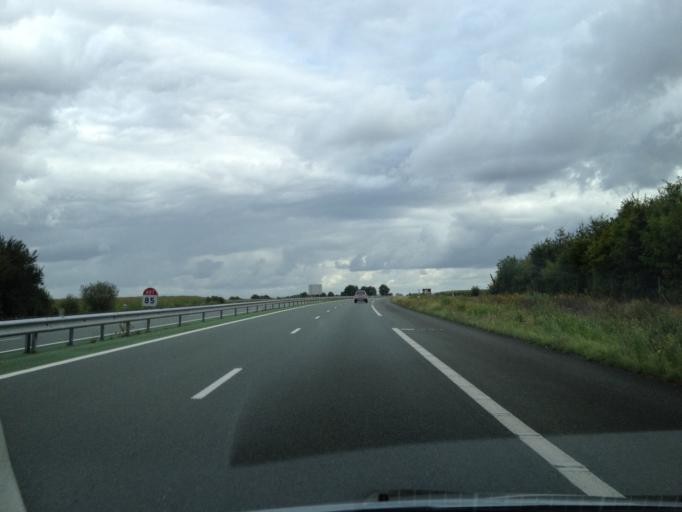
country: FR
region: Pays de la Loire
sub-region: Departement de la Vendee
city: Saint-Fulgent
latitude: 46.8571
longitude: -1.1428
